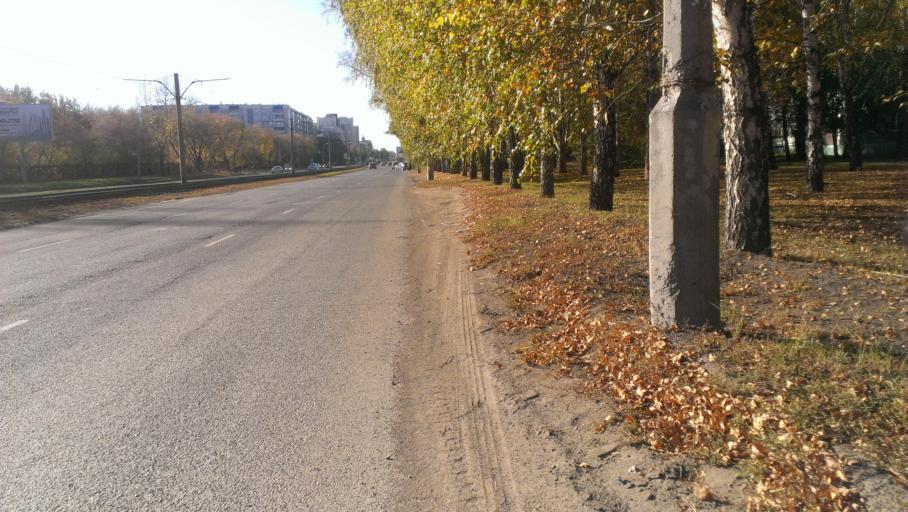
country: RU
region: Altai Krai
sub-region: Gorod Barnaulskiy
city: Barnaul
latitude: 53.3610
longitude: 83.6869
